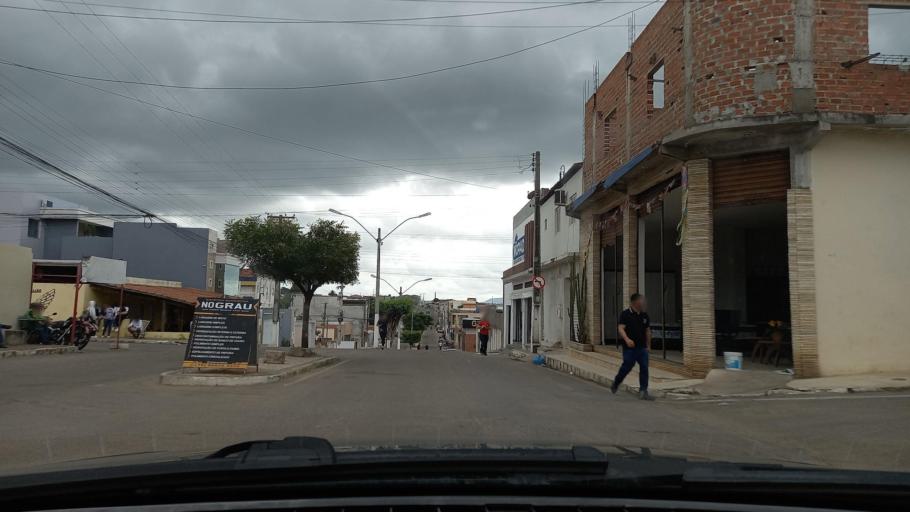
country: BR
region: Sergipe
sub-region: Caninde De Sao Francisco
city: Caninde de Sao Francisco
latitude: -9.6621
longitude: -37.7884
